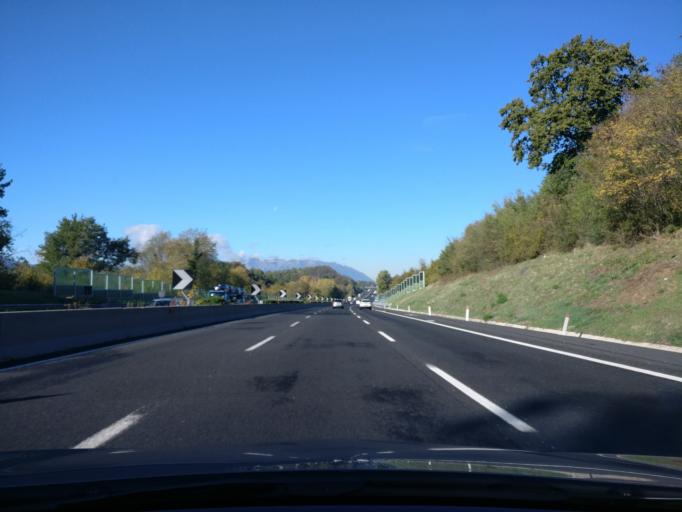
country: IT
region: Latium
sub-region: Provincia di Frosinone
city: Pofi
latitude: 41.5587
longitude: 13.4112
